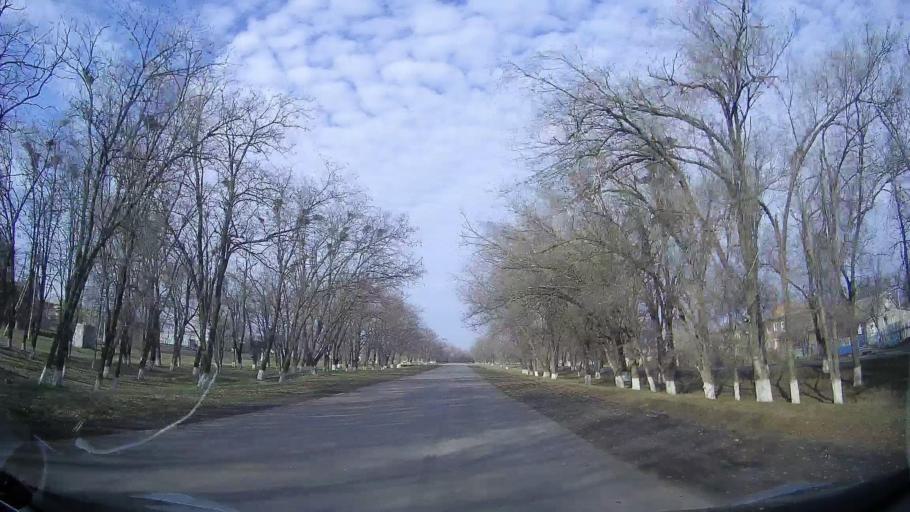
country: RU
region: Rostov
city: Gigant
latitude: 46.8370
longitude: 41.3328
